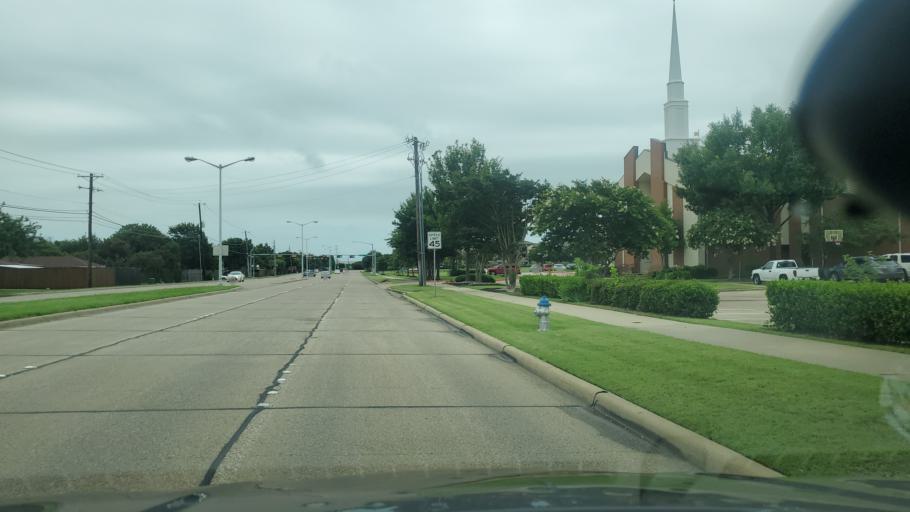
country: US
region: Texas
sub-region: Dallas County
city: Garland
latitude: 32.9386
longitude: -96.6349
